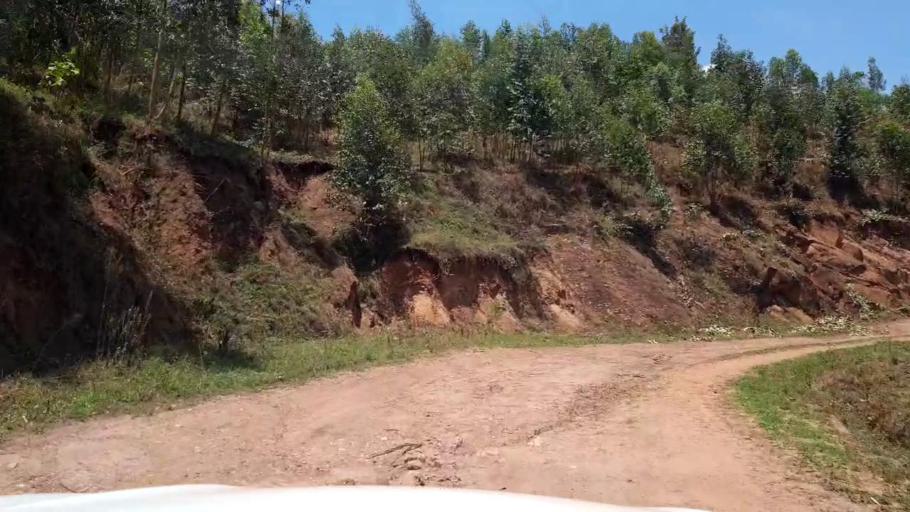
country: RW
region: Northern Province
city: Byumba
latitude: -1.5262
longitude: 30.1748
